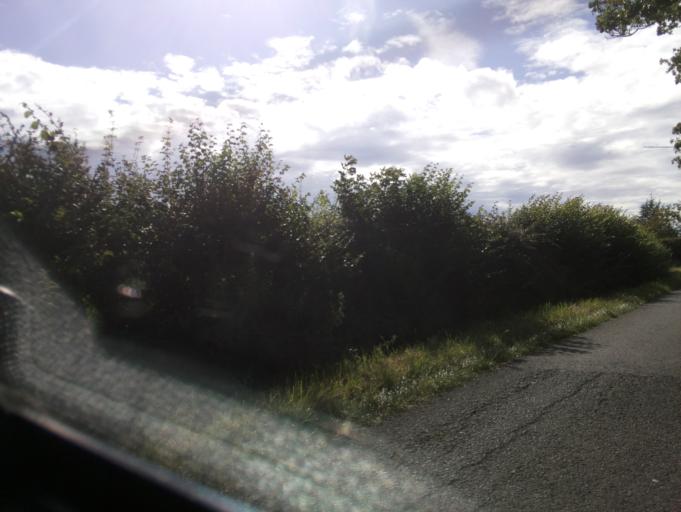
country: GB
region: England
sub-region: Gloucestershire
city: Stonehouse
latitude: 51.7999
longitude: -2.2619
